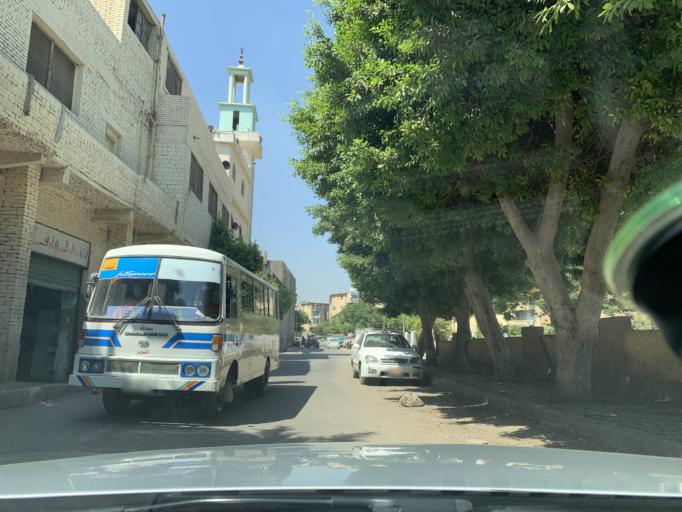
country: EG
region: Muhafazat al Qahirah
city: Cairo
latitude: 30.0717
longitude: 31.2561
